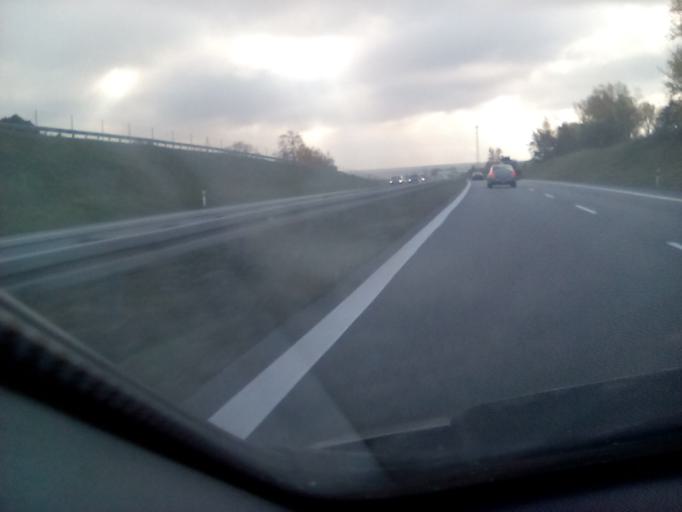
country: PL
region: Masovian Voivodeship
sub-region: Powiat bialobrzeski
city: Promna
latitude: 51.6823
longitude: 20.9379
